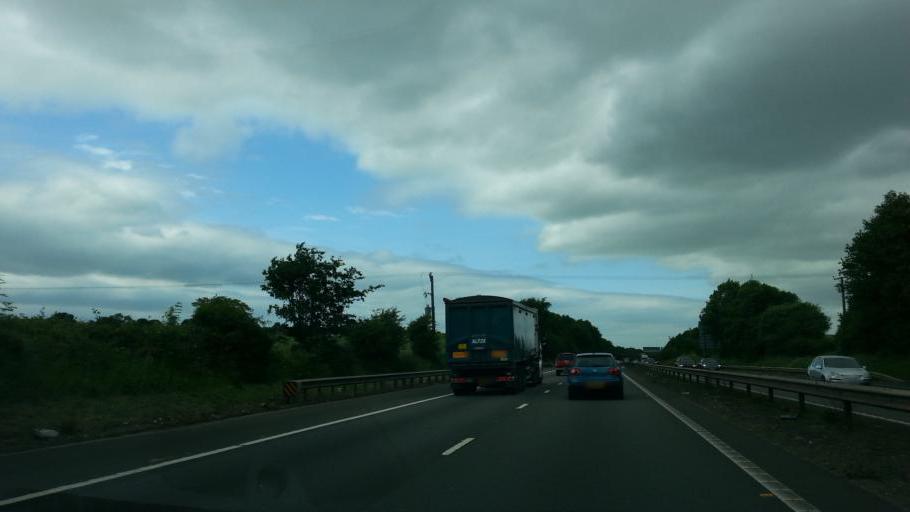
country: GB
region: England
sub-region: Staffordshire
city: Fazeley
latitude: 52.6140
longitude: -1.6338
